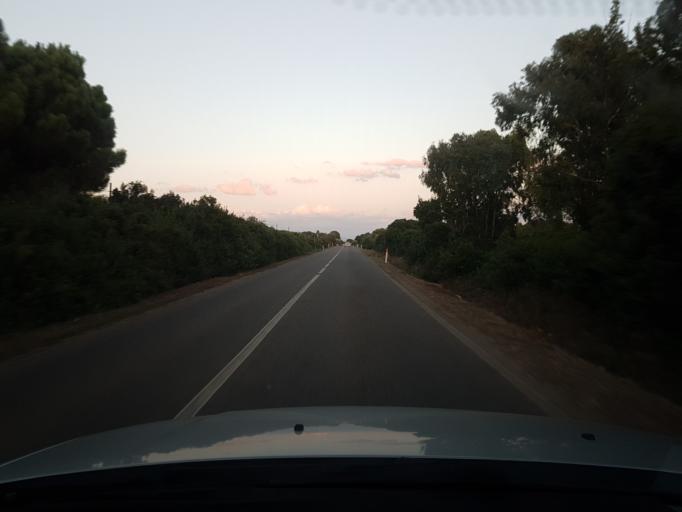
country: IT
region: Sardinia
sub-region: Provincia di Oristano
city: Riola Sardo
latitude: 40.0237
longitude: 8.4451
